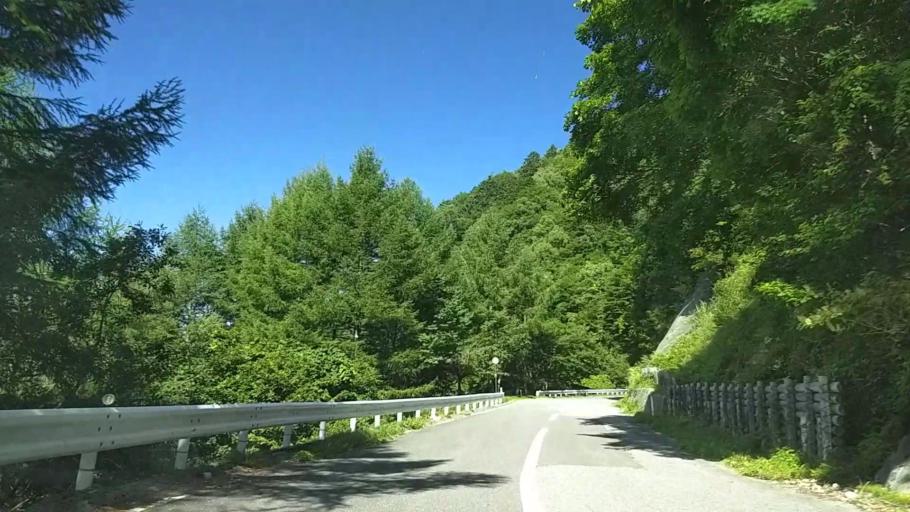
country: JP
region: Nagano
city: Matsumoto
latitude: 36.1953
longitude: 138.1182
